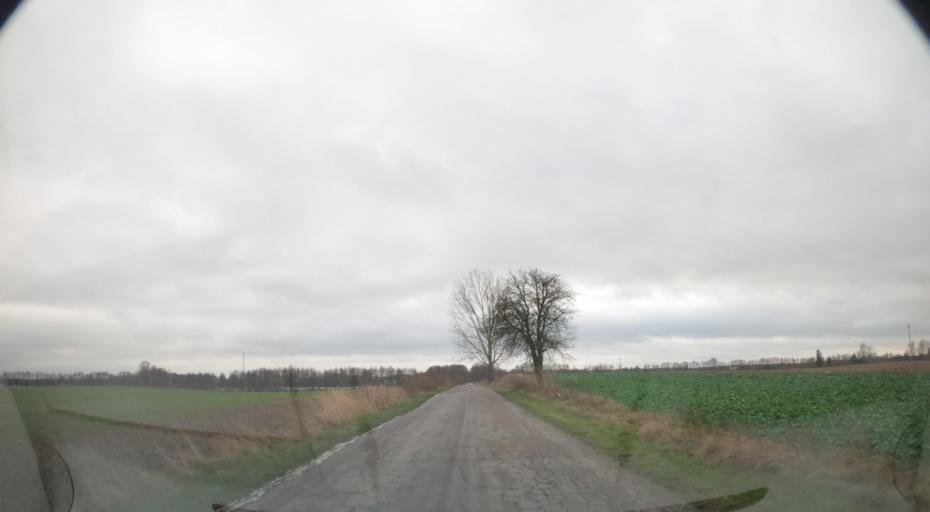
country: PL
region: Greater Poland Voivodeship
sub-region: Powiat pilski
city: Wysoka
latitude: 53.2607
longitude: 17.1153
